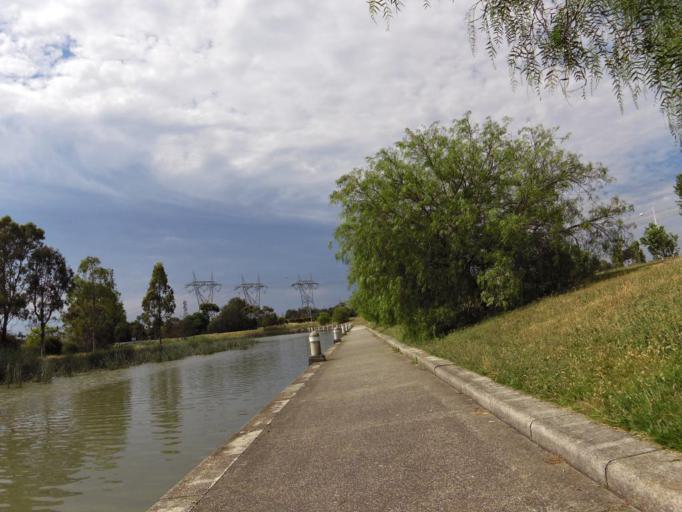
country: AU
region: Victoria
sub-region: Whittlesea
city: Mill Park
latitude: -37.6399
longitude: 145.0684
